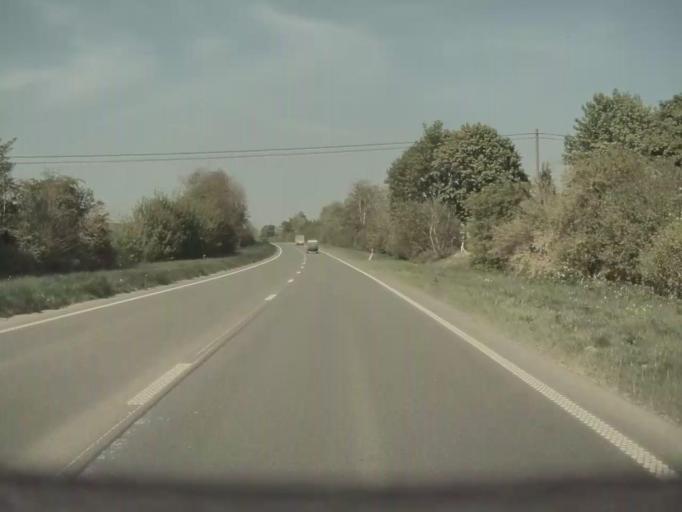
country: BE
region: Wallonia
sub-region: Province de Namur
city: Ciney
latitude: 50.2990
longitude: 5.1192
